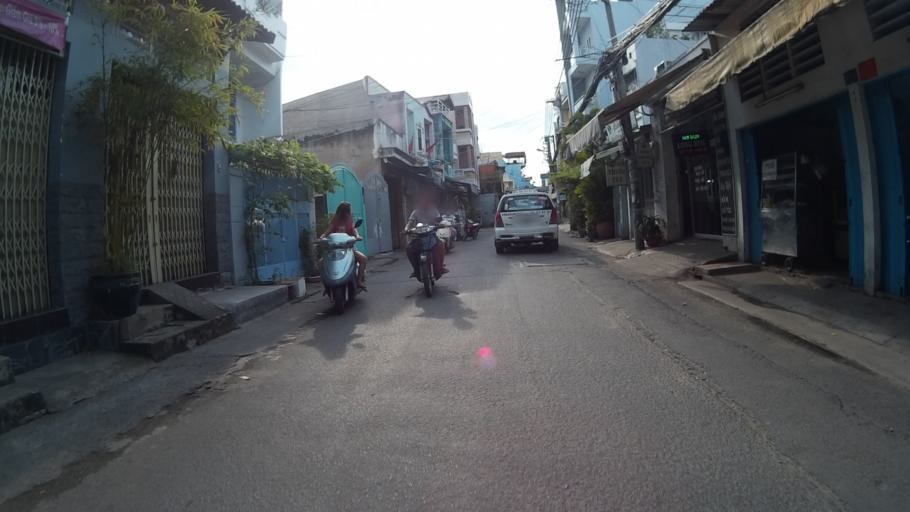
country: VN
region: Ho Chi Minh City
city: Quan Binh Thanh
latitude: 10.7993
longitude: 106.7006
